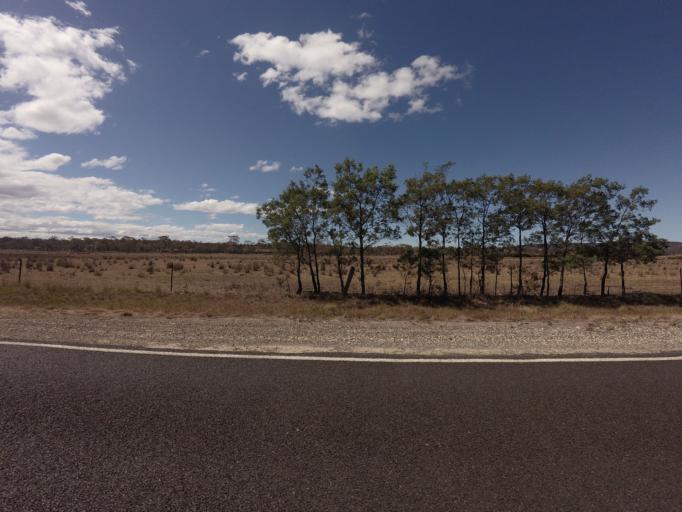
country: AU
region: Tasmania
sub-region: Break O'Day
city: St Helens
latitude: -42.0439
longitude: 148.0367
